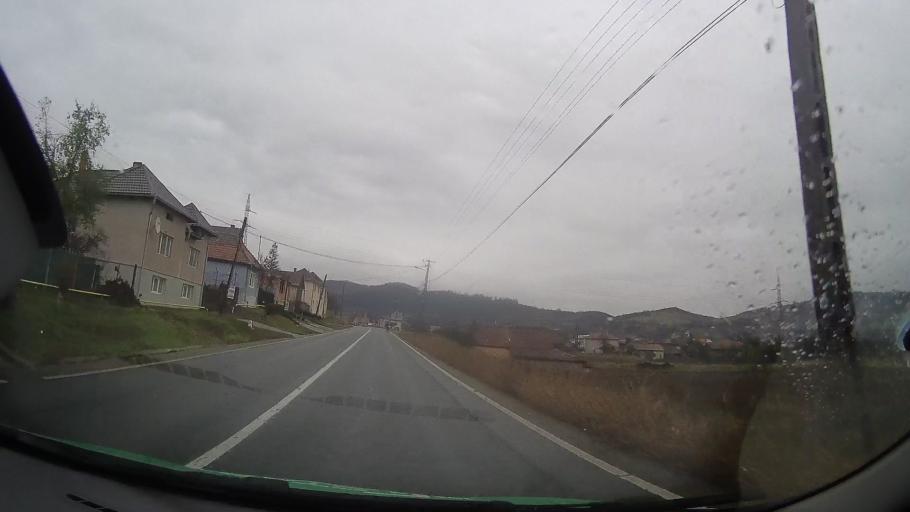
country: RO
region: Bistrita-Nasaud
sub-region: Comuna Teaca
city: Teaca
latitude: 46.9144
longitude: 24.4972
